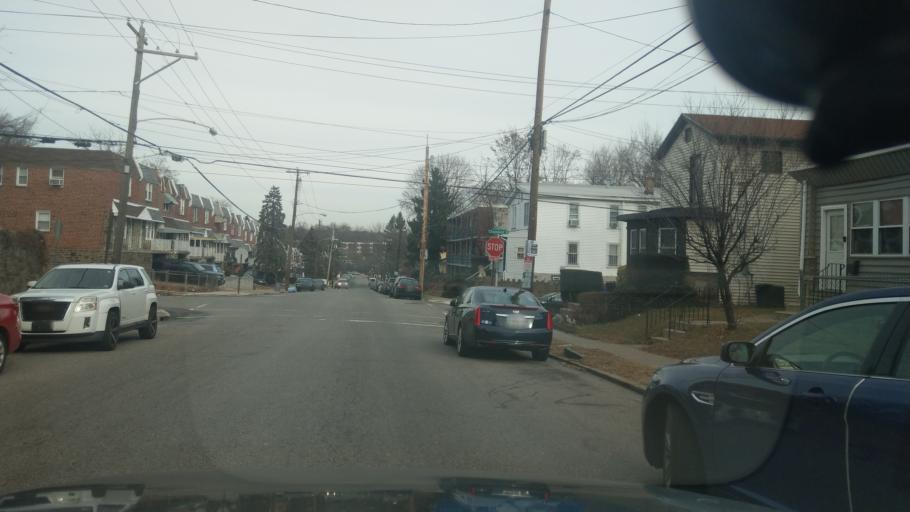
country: US
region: Pennsylvania
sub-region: Montgomery County
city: Wyncote
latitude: 40.0432
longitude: -75.1367
